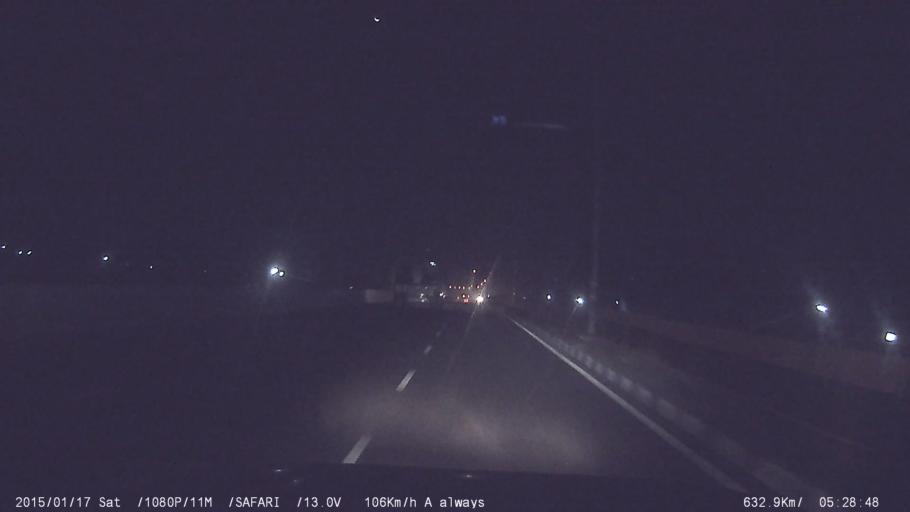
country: IN
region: Tamil Nadu
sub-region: Vellore
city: Arcot
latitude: 12.9222
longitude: 79.2769
